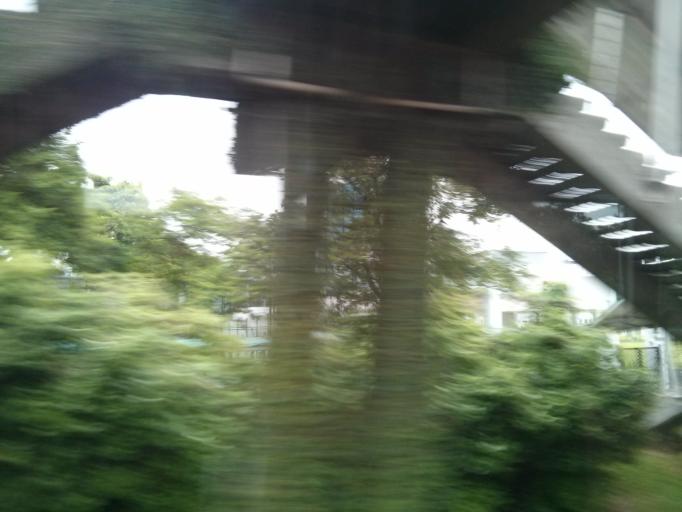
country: SG
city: Singapore
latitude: 1.3002
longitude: 103.7788
